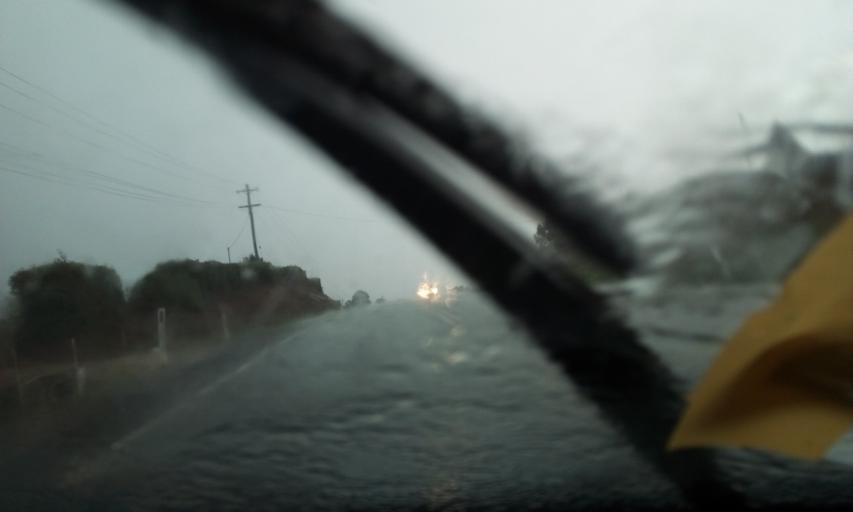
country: AU
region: New South Wales
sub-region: Wollondilly
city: Douglas Park
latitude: -34.1593
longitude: 150.7211
